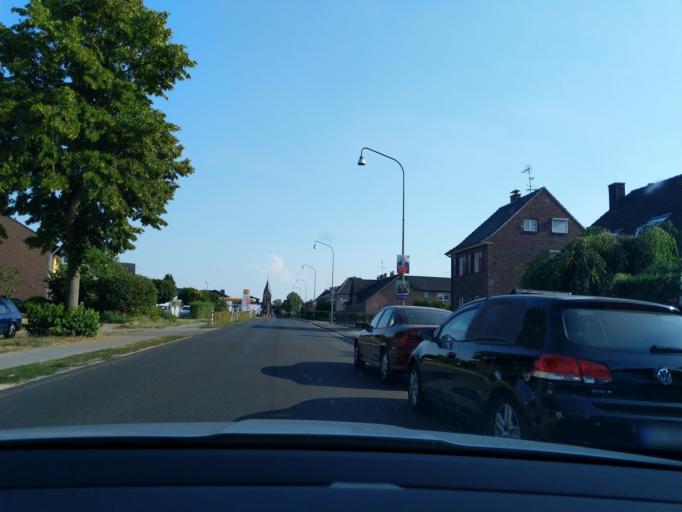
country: DE
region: North Rhine-Westphalia
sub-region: Regierungsbezirk Koln
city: Wassenberg
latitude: 51.1278
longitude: 6.1914
